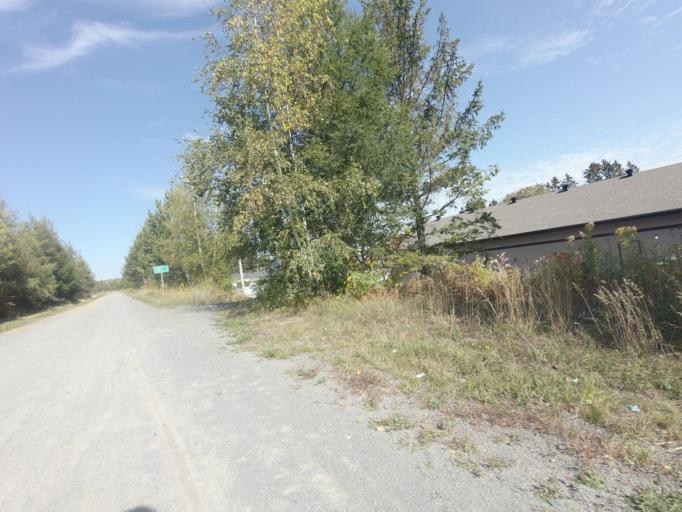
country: CA
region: Quebec
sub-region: Laurentides
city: Sainte-Agathe-des-Monts
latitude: 46.0524
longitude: -74.2825
